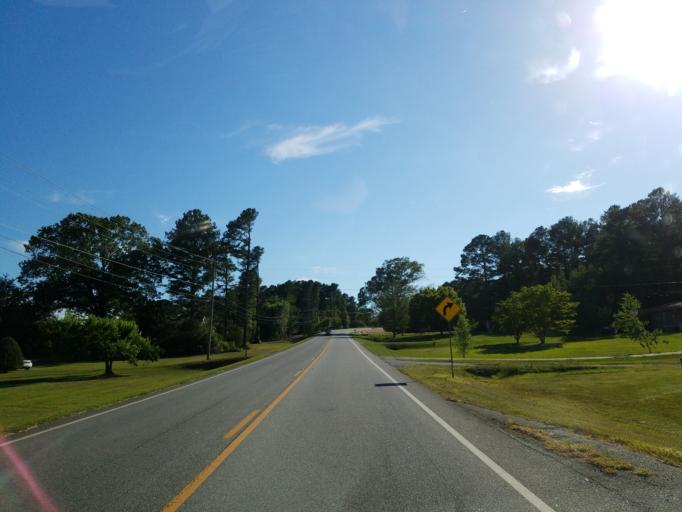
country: US
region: Georgia
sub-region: Gordon County
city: Calhoun
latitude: 34.5731
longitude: -84.9686
